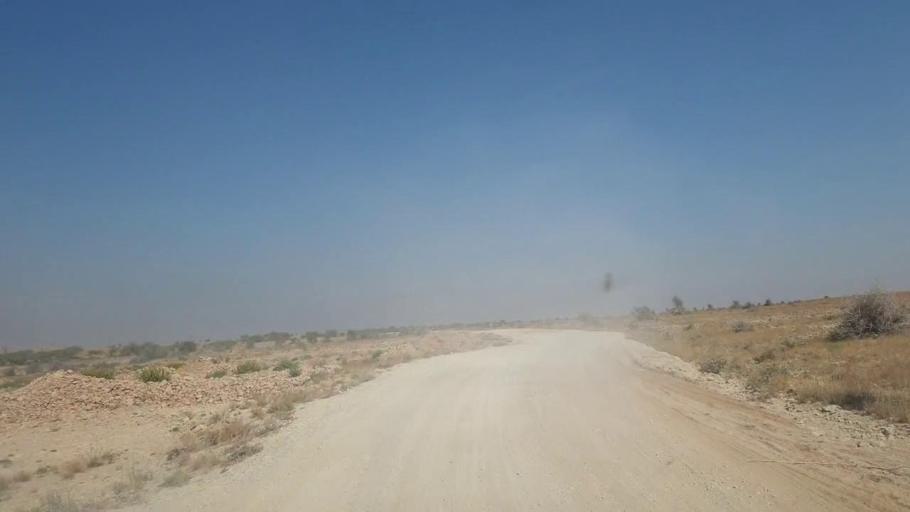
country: PK
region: Sindh
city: Thatta
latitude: 25.2294
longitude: 67.8036
